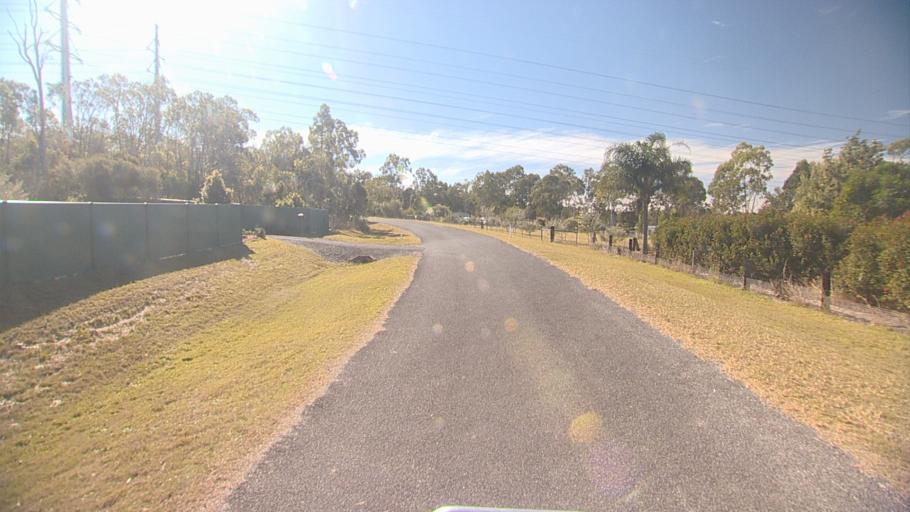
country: AU
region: Queensland
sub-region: Ipswich
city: Springfield Lakes
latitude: -27.7238
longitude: 152.9388
